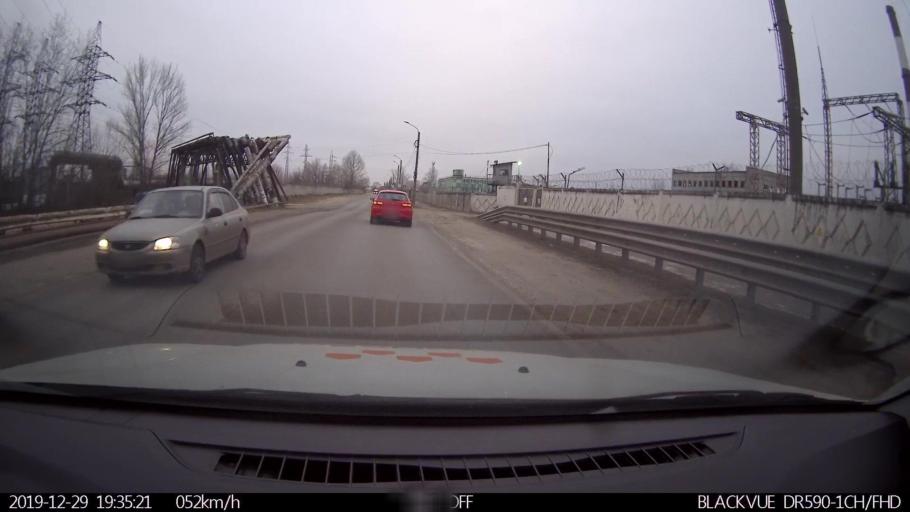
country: RU
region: Nizjnij Novgorod
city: Neklyudovo
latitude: 56.3513
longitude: 43.8944
